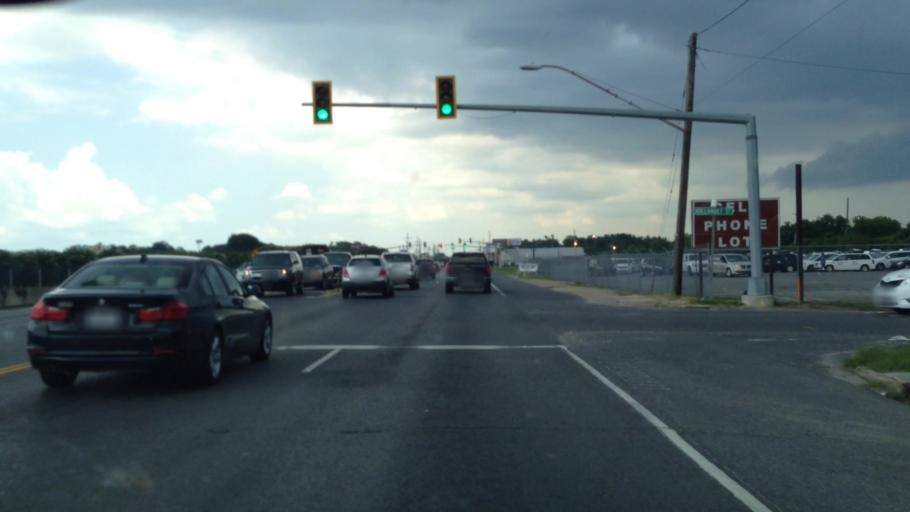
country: US
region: Louisiana
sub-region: Jefferson Parish
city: Kenner
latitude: 29.9816
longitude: -90.2539
